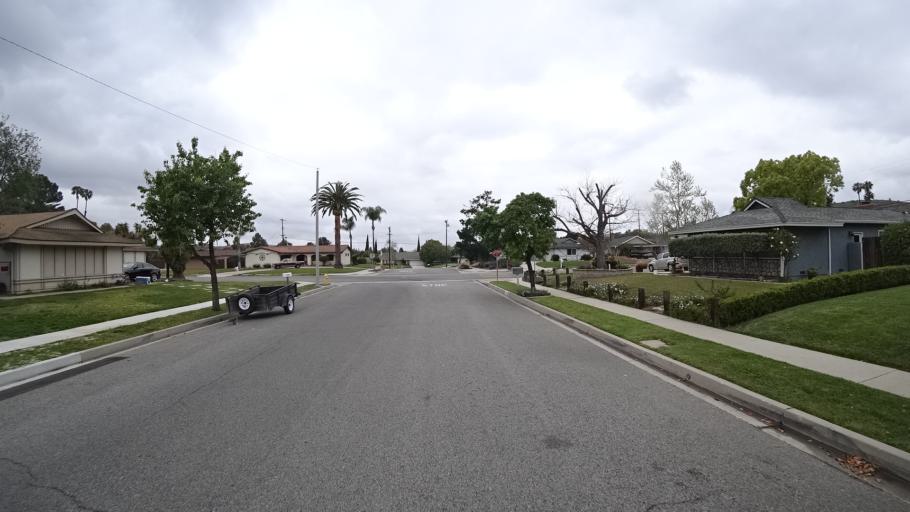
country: US
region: California
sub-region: Ventura County
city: Thousand Oaks
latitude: 34.2155
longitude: -118.8823
